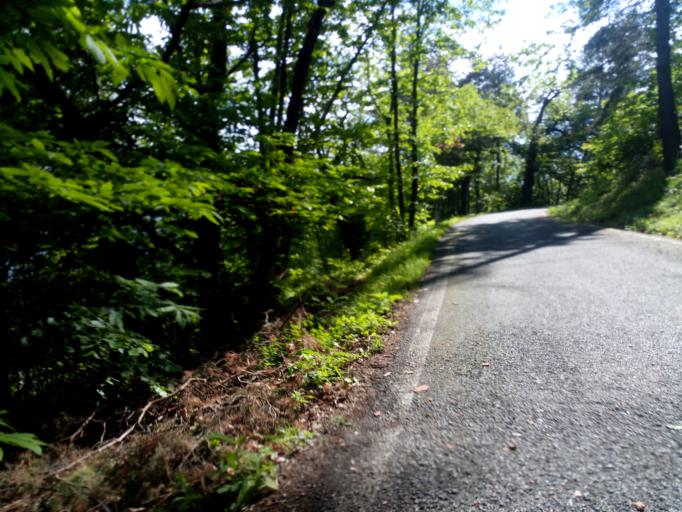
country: IT
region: Piedmont
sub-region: Provincia di Torino
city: Meana di Susa
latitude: 45.1177
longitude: 7.0634
